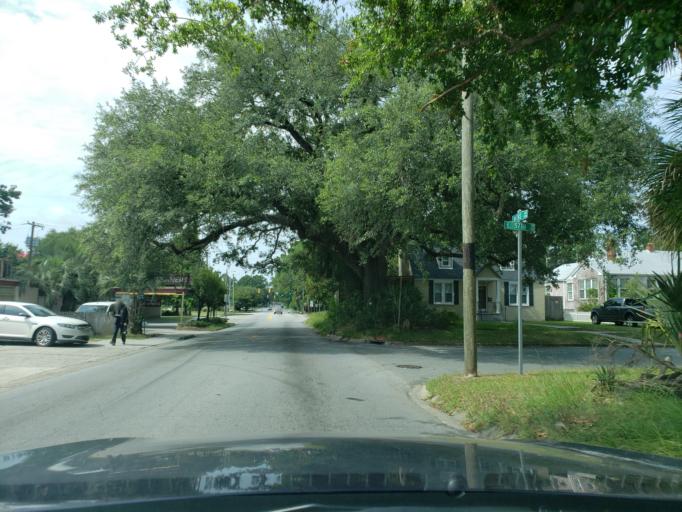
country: US
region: Georgia
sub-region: Chatham County
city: Thunderbolt
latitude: 32.0376
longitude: -81.0897
